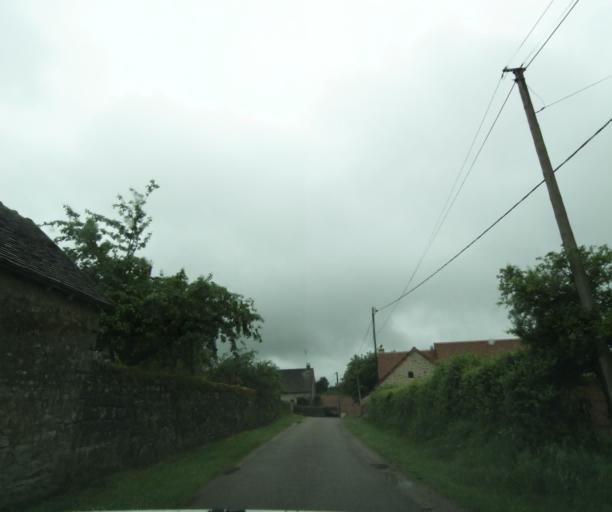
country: FR
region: Bourgogne
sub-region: Departement de Saone-et-Loire
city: Charolles
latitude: 46.4138
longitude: 4.3050
